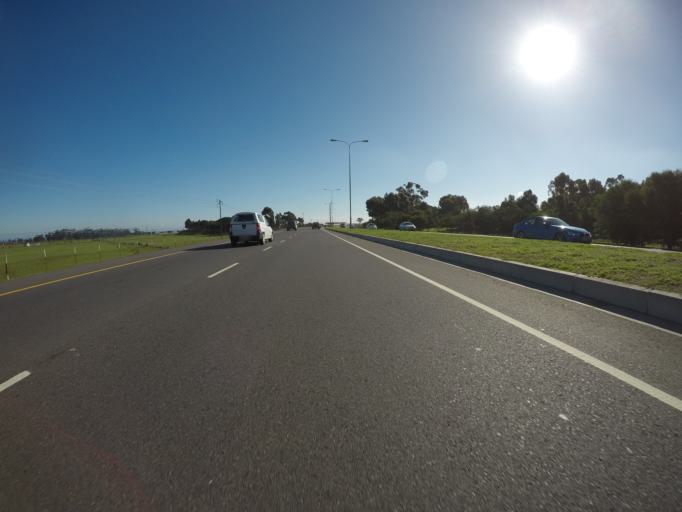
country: ZA
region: Western Cape
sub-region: Overberg District Municipality
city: Grabouw
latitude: -34.1236
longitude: 18.8877
